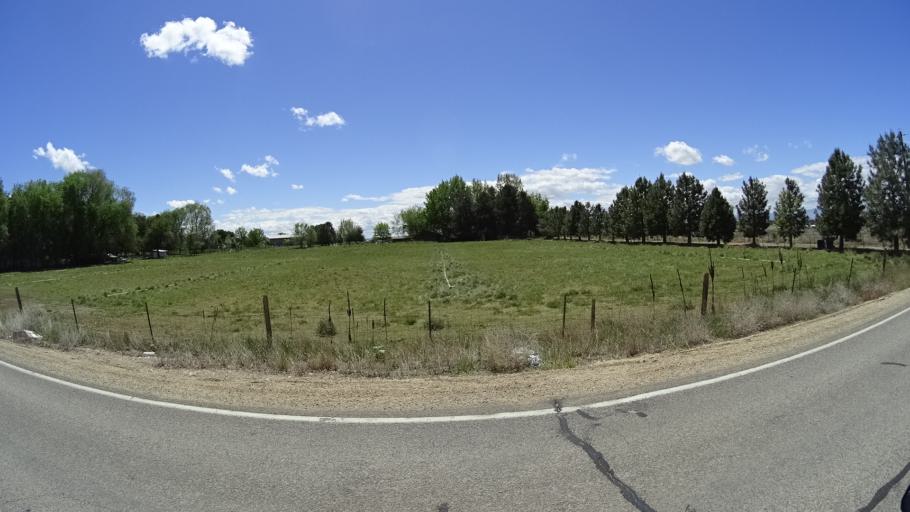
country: US
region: Idaho
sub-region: Ada County
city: Kuna
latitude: 43.5466
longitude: -116.4033
